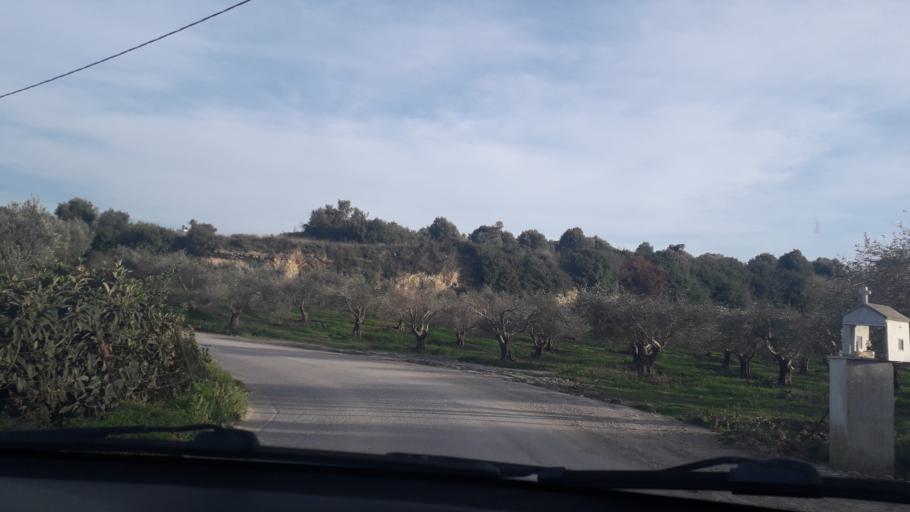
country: GR
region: Crete
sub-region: Nomos Rethymnis
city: Panormos
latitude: 35.3856
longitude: 24.6154
